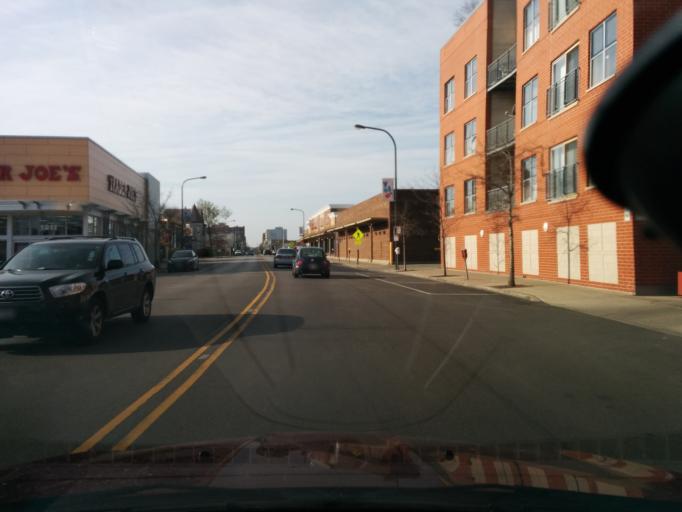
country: US
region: Illinois
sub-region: Cook County
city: Evanston
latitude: 42.0403
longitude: -87.6806
